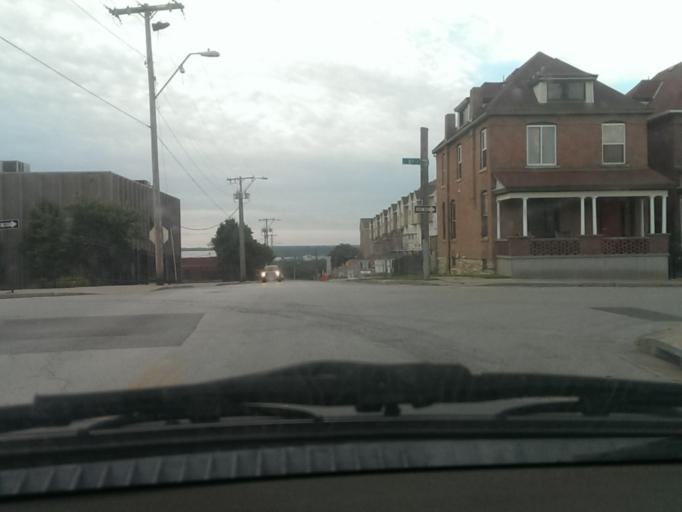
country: US
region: Missouri
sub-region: Jackson County
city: Kansas City
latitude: 39.1039
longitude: -94.5697
